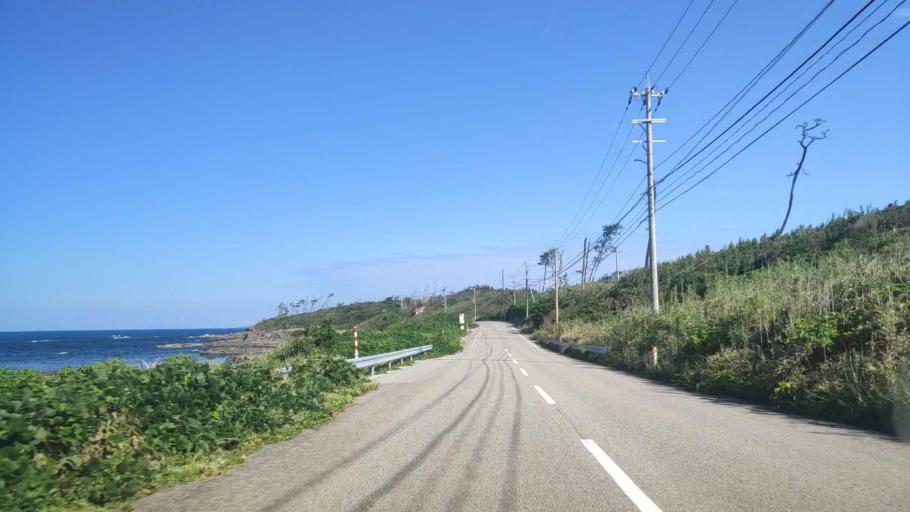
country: JP
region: Ishikawa
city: Hakui
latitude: 37.0663
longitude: 136.7227
